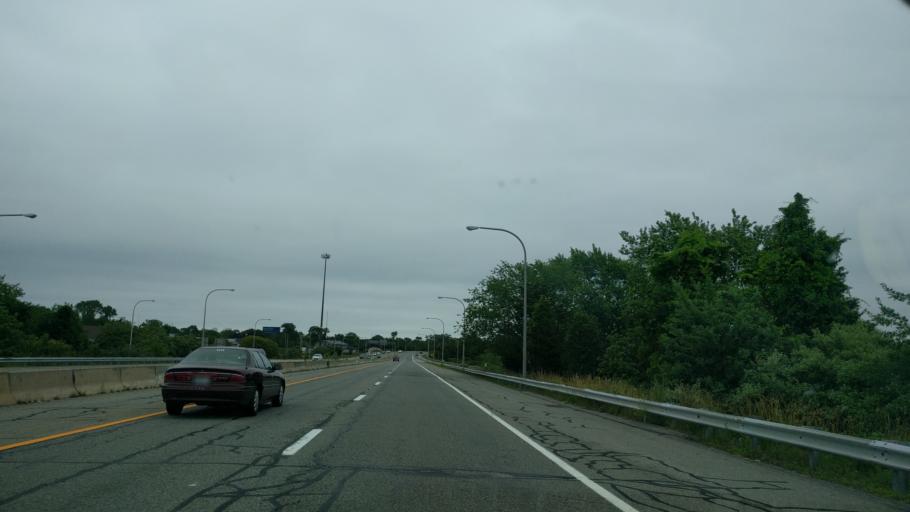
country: US
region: Rhode Island
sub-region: Newport County
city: Portsmouth
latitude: 41.6292
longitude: -71.2431
